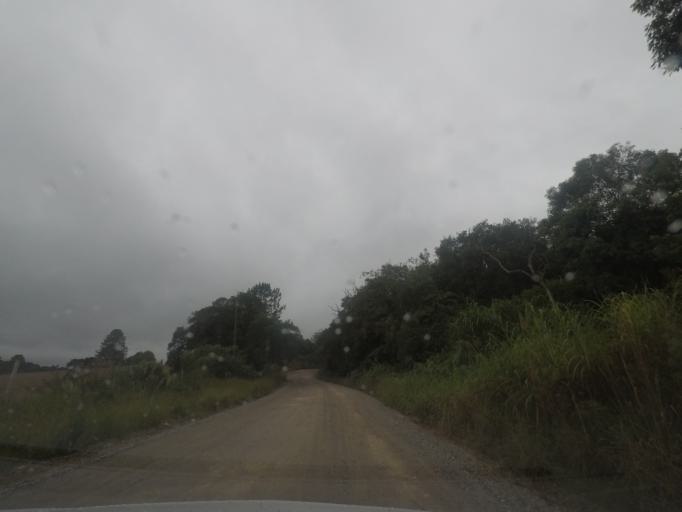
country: BR
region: Parana
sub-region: Campina Grande Do Sul
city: Campina Grande do Sul
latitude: -25.3105
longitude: -49.0934
